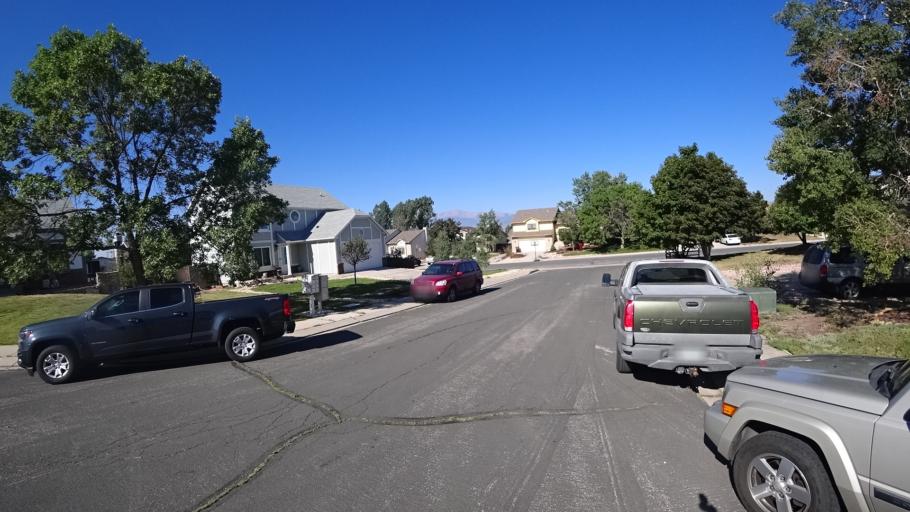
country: US
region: Colorado
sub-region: El Paso County
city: Black Forest
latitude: 38.9583
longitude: -104.7469
